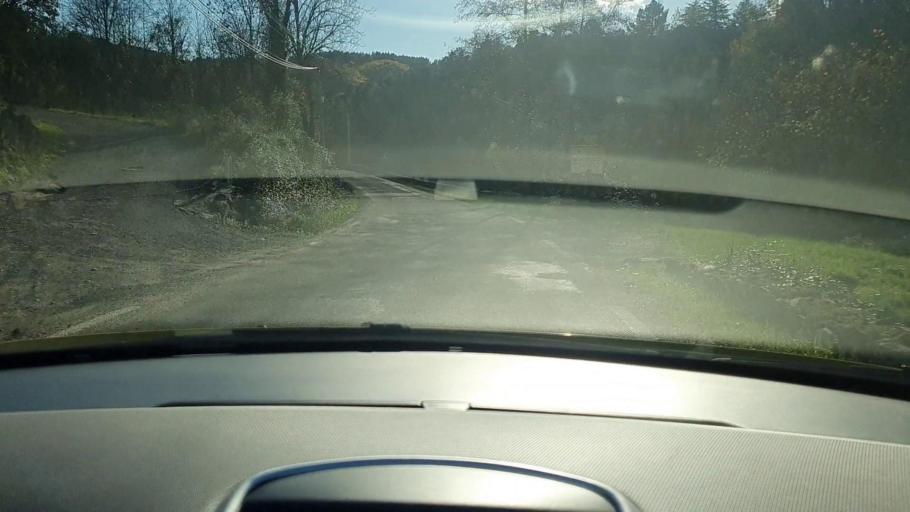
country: FR
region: Languedoc-Roussillon
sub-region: Departement du Gard
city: Lasalle
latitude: 44.0512
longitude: 3.8408
